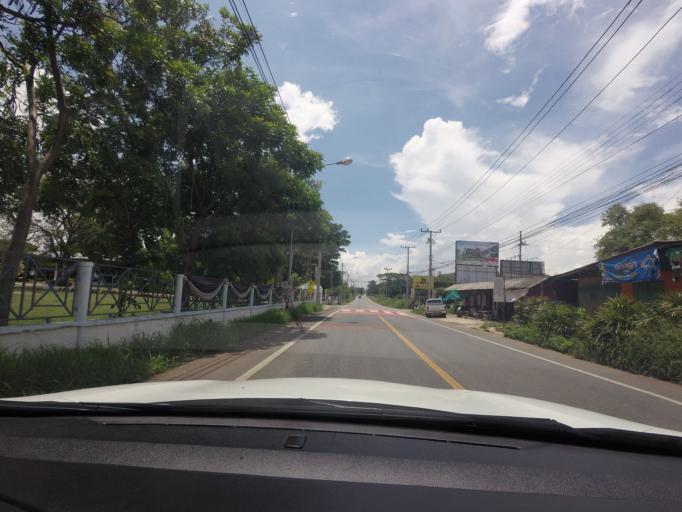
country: TH
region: Sara Buri
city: Muak Lek
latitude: 14.6028
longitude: 101.2140
